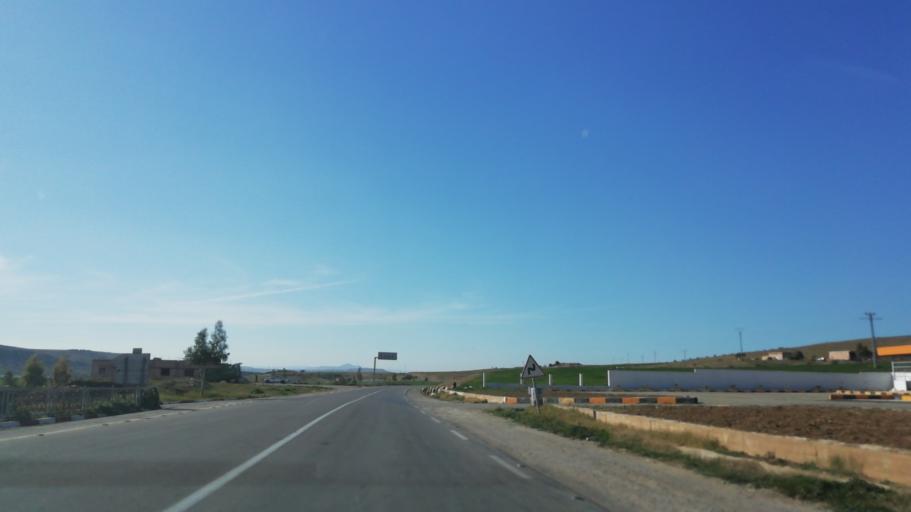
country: DZ
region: Mascara
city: Oued el Abtal
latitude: 35.4512
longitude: 0.7809
